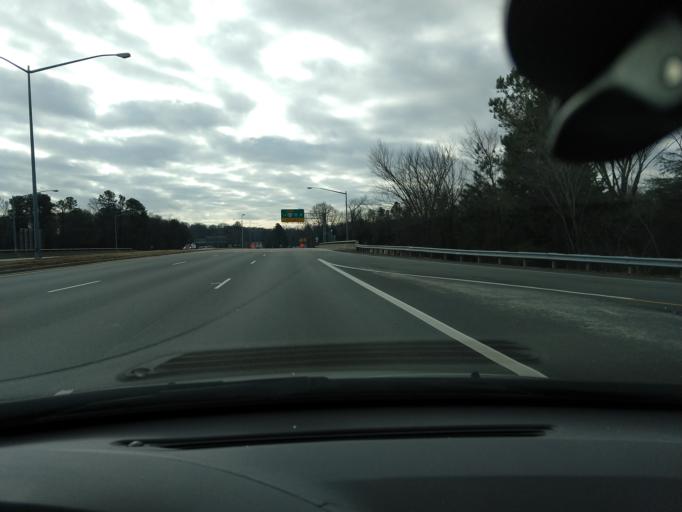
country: US
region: Virginia
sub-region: Chesterfield County
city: Bensley
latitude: 37.4444
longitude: -77.4405
